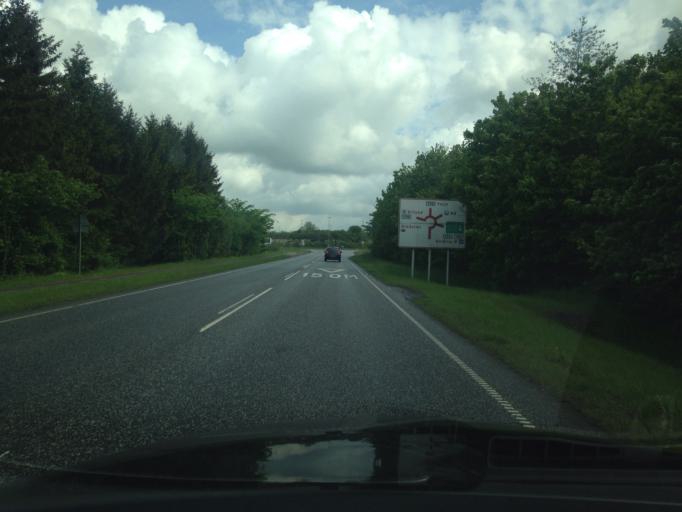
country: DK
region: South Denmark
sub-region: Kolding Kommune
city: Kolding
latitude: 55.5425
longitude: 9.4756
